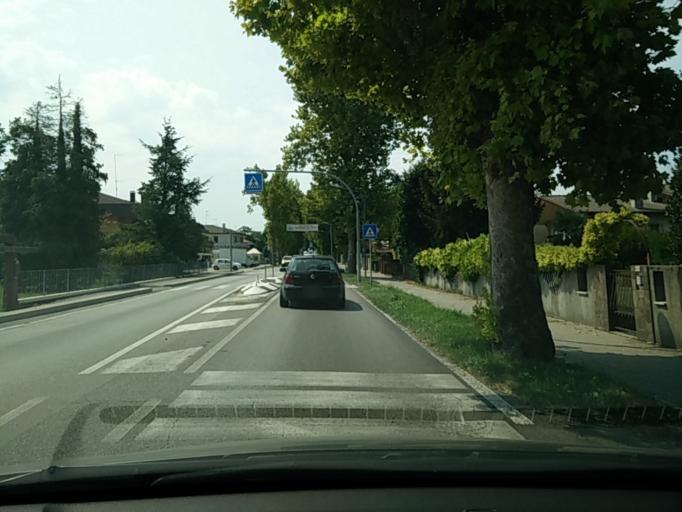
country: IT
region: Veneto
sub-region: Provincia di Venezia
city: Eraclea
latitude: 45.5778
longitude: 12.6771
